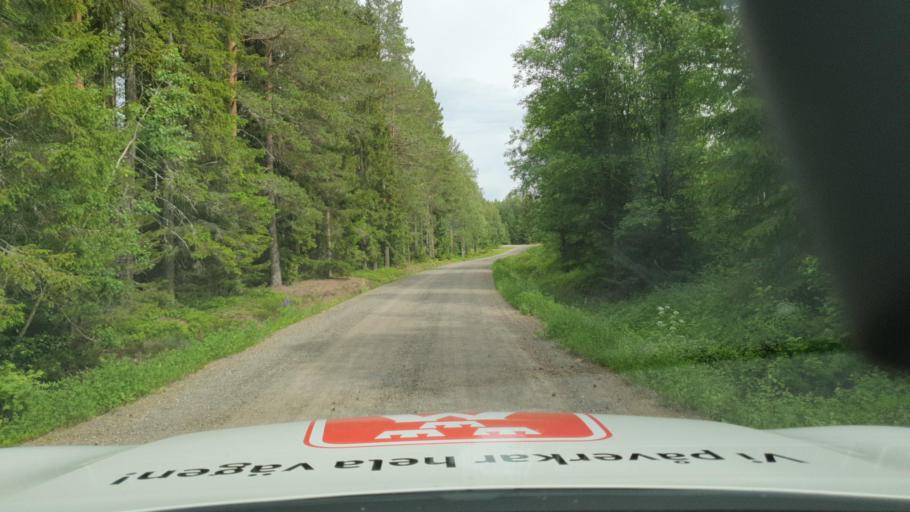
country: SE
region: Vaesterbotten
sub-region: Robertsfors Kommun
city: Robertsfors
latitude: 64.2614
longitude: 20.6619
